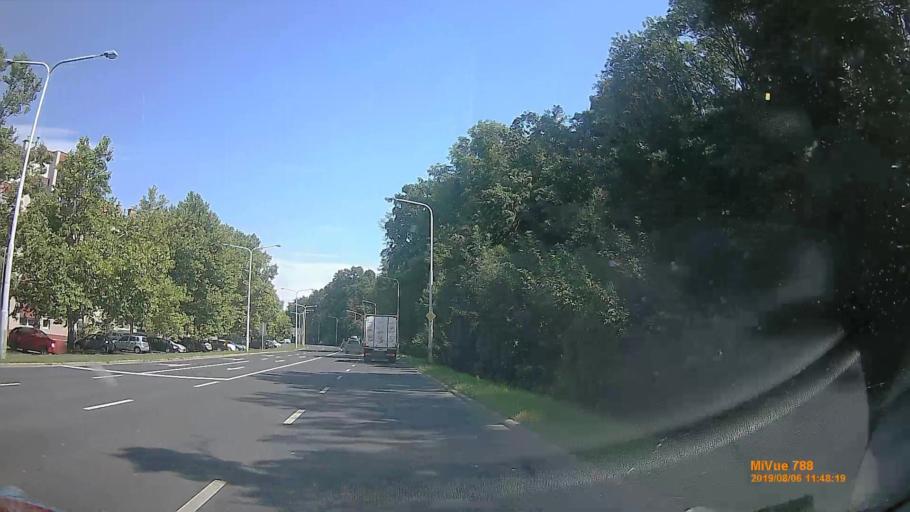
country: HU
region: Vas
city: Kormend
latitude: 47.0122
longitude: 16.6082
